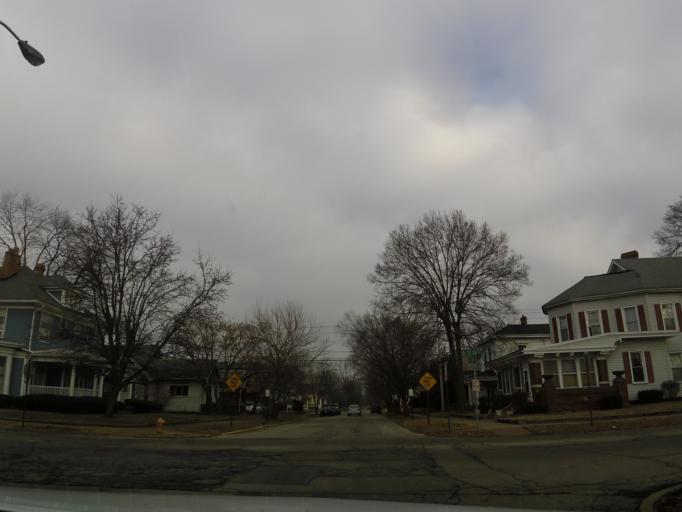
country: US
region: Indiana
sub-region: Bartholomew County
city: Columbus
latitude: 39.2093
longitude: -85.9201
